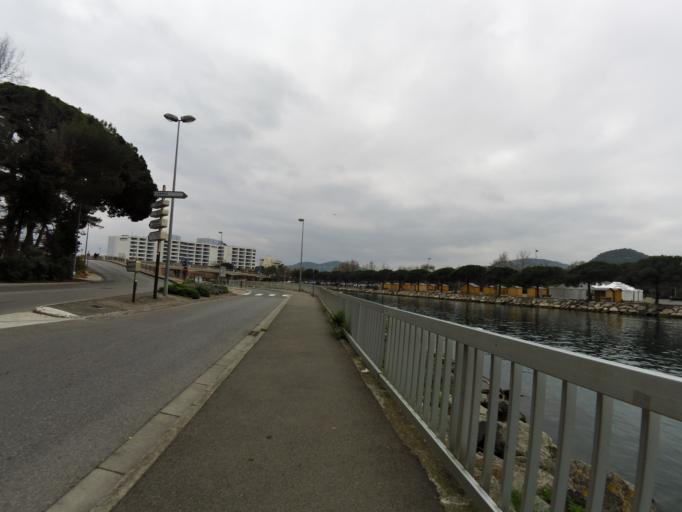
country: FR
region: Provence-Alpes-Cote d'Azur
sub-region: Departement des Alpes-Maritimes
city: Mandelieu-la-Napoule
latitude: 43.5324
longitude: 6.9470
